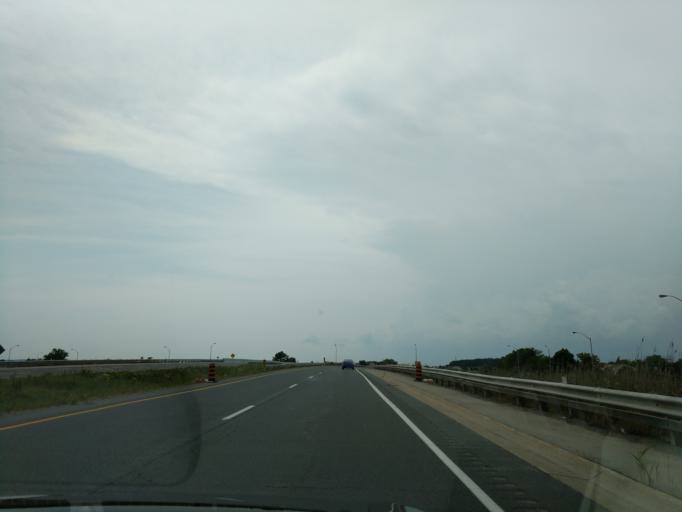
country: CA
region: Ontario
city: Thorold
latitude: 43.1151
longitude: -79.2134
